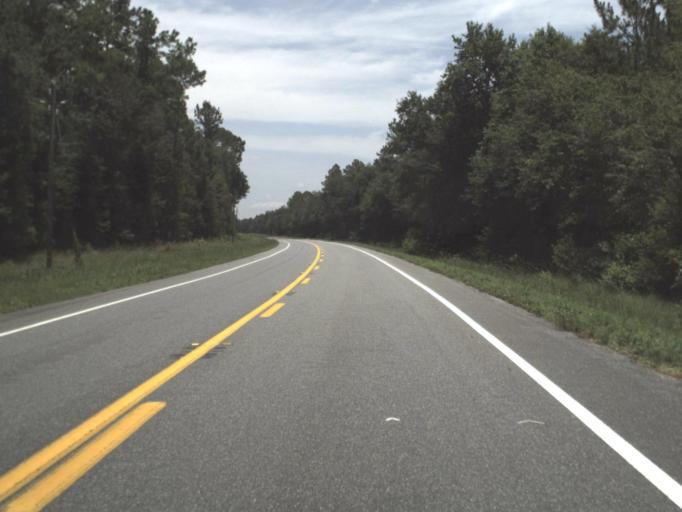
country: US
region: Florida
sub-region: Lafayette County
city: Mayo
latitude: 29.9782
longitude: -83.2027
